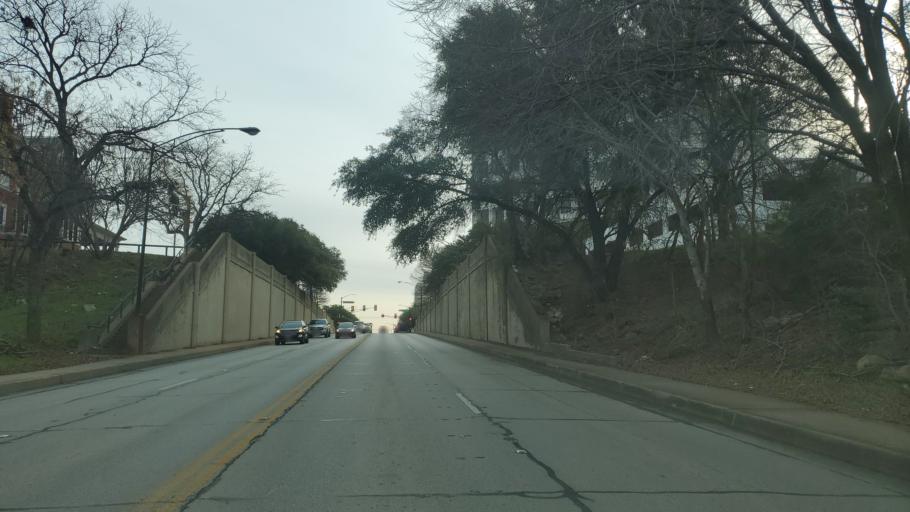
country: US
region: Texas
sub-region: Tarrant County
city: Fort Worth
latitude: 32.7467
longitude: -97.3435
